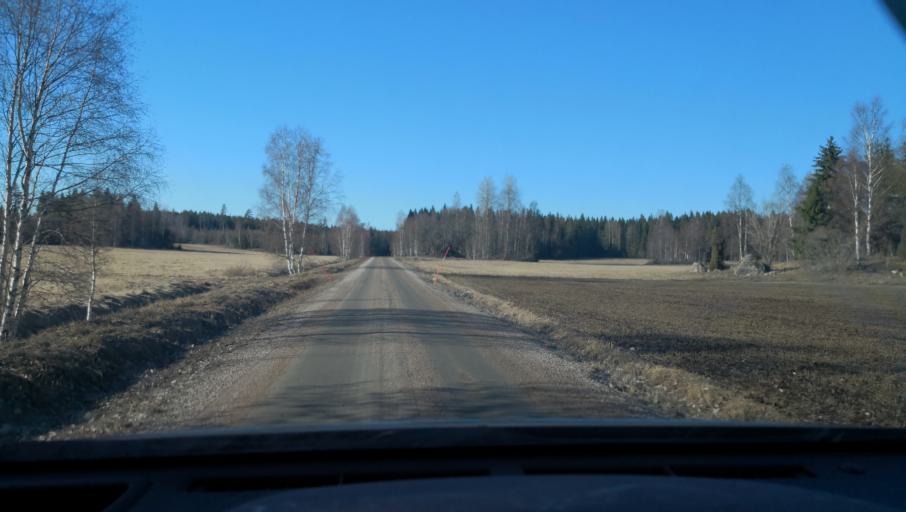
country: SE
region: Vaestmanland
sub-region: Sala Kommun
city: Sala
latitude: 60.1313
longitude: 16.6521
